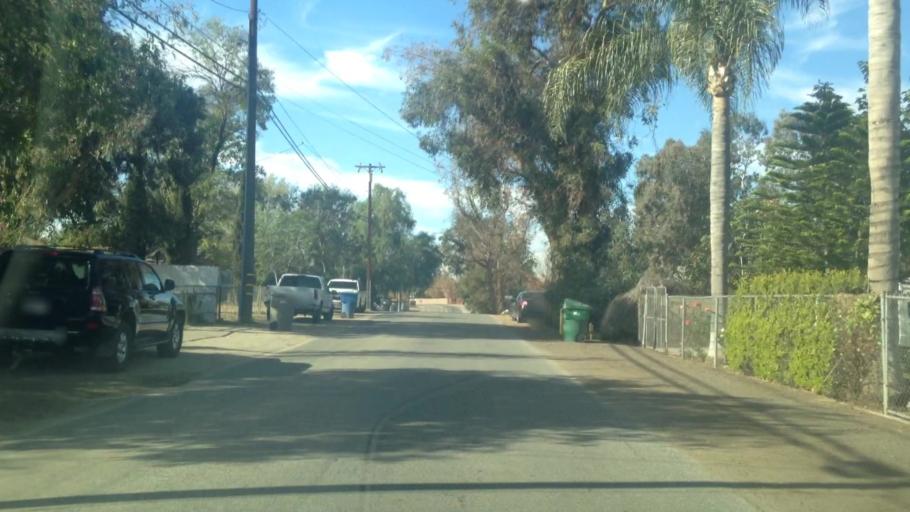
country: US
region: California
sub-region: Riverside County
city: Mira Loma
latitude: 33.9733
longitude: -117.5218
